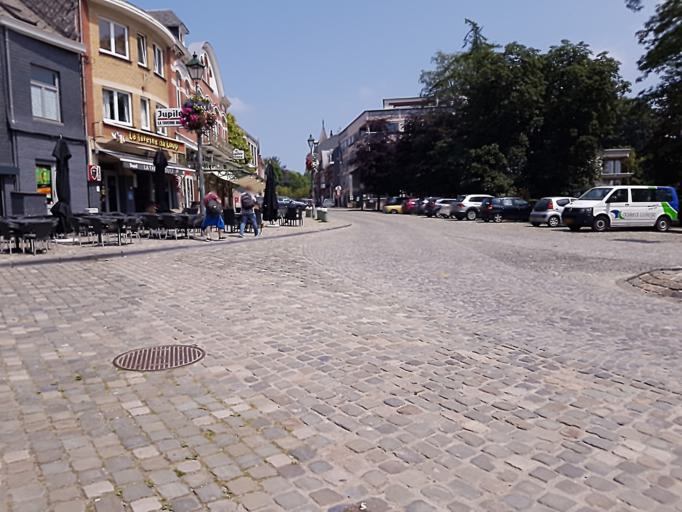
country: BE
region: Wallonia
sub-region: Province de Liege
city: Stavelot
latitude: 50.3949
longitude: 5.9317
